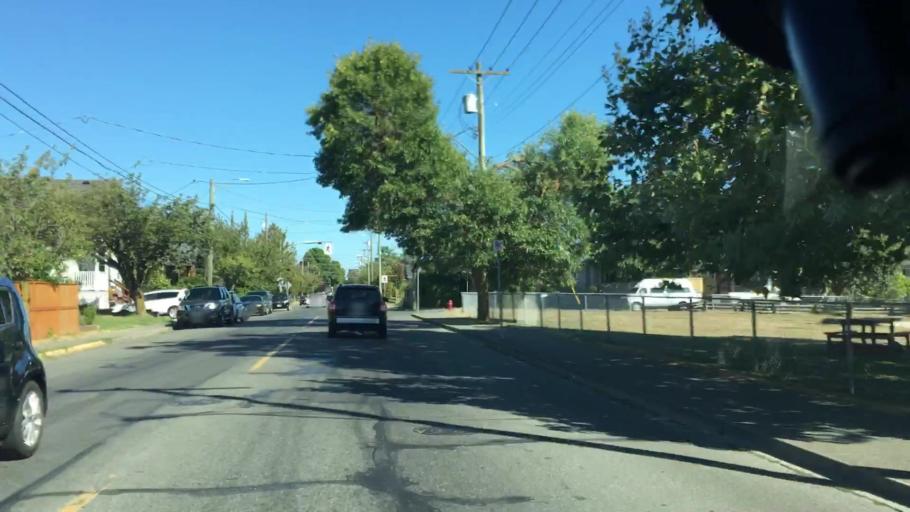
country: CA
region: British Columbia
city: Victoria
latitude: 48.4344
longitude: -123.3438
